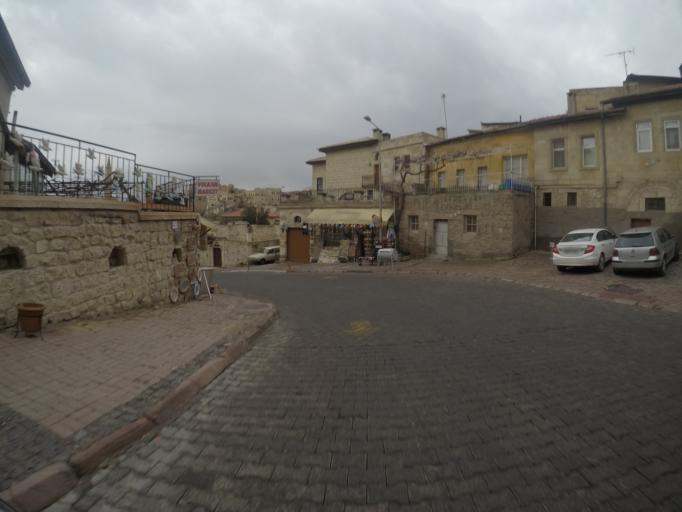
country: TR
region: Nevsehir
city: Urgub
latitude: 38.6326
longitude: 34.9085
